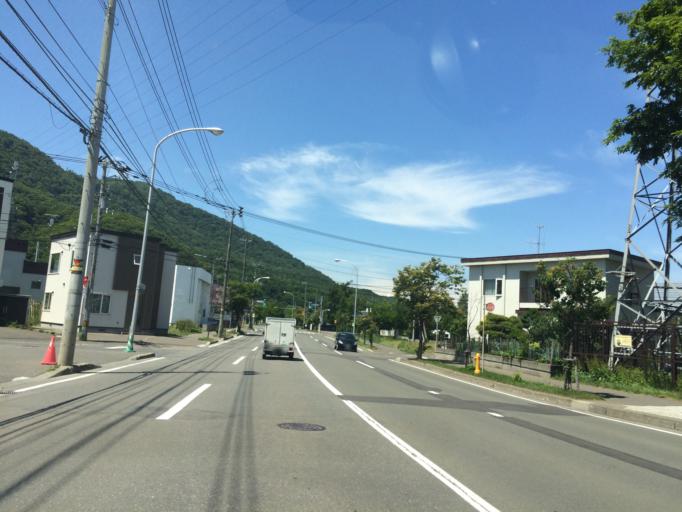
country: JP
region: Hokkaido
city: Sapporo
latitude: 43.0176
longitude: 141.3505
